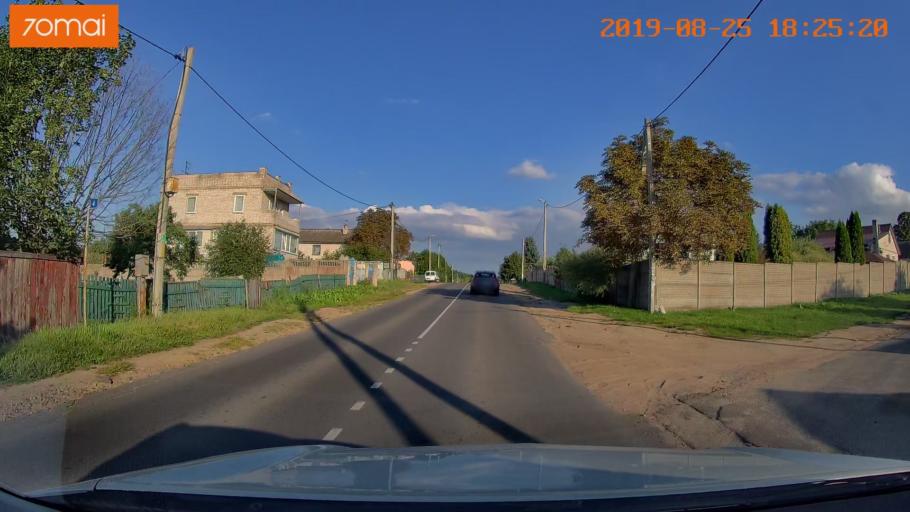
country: BY
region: Minsk
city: Khatsyezhyna
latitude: 53.9370
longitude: 27.3458
